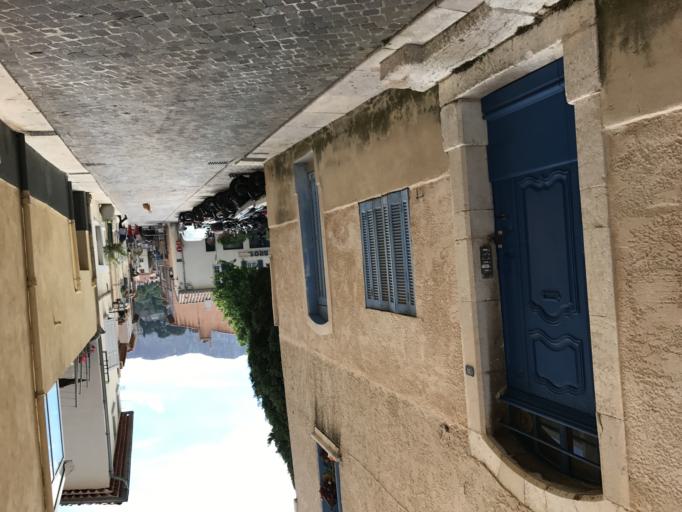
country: FR
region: Provence-Alpes-Cote d'Azur
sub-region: Departement des Bouches-du-Rhone
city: Cassis
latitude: 43.2158
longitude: 5.5376
